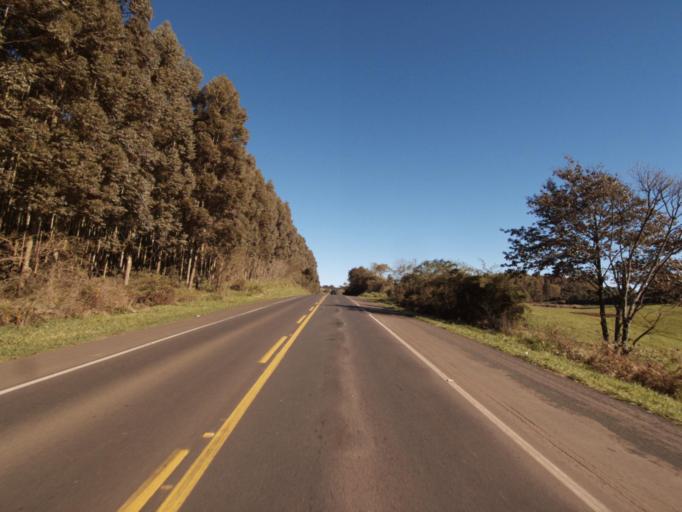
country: BR
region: Santa Catarina
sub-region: Xanxere
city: Xanxere
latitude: -26.9199
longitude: -52.4948
